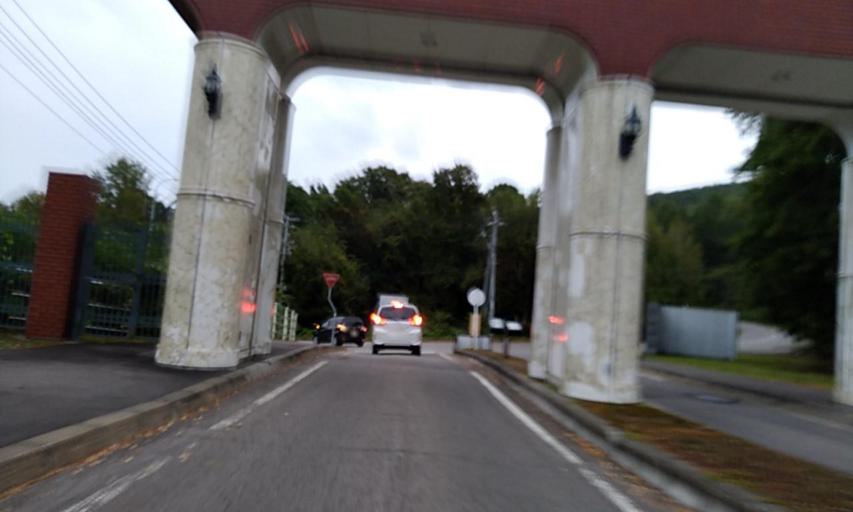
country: JP
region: Hokkaido
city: Abashiri
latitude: 43.9974
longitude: 144.2286
